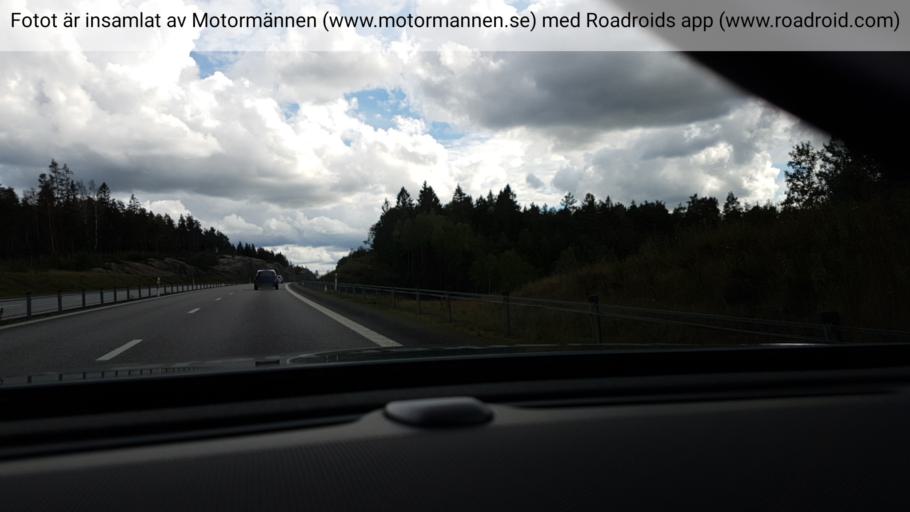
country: SE
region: Vaestra Goetaland
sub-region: Lilla Edets Kommun
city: Lodose
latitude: 58.0604
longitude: 12.1664
